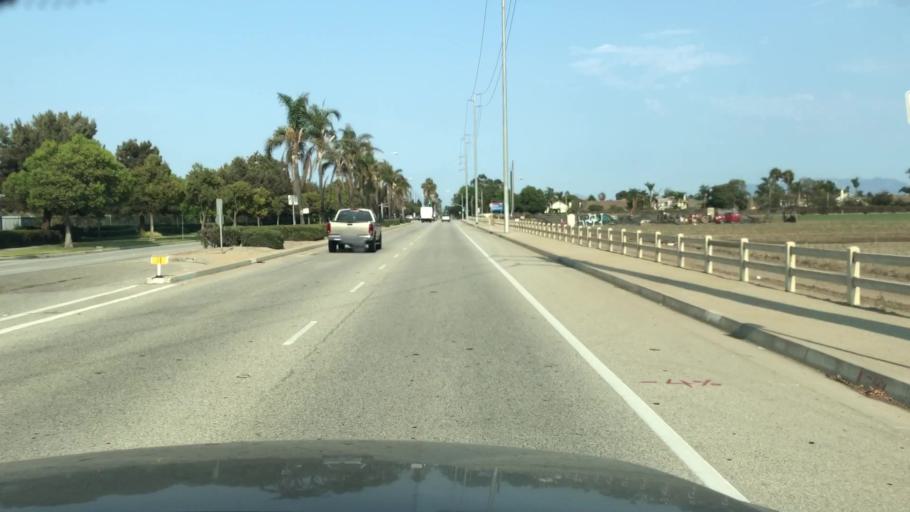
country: US
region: California
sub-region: Ventura County
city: Oxnard
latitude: 34.2193
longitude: -119.2101
